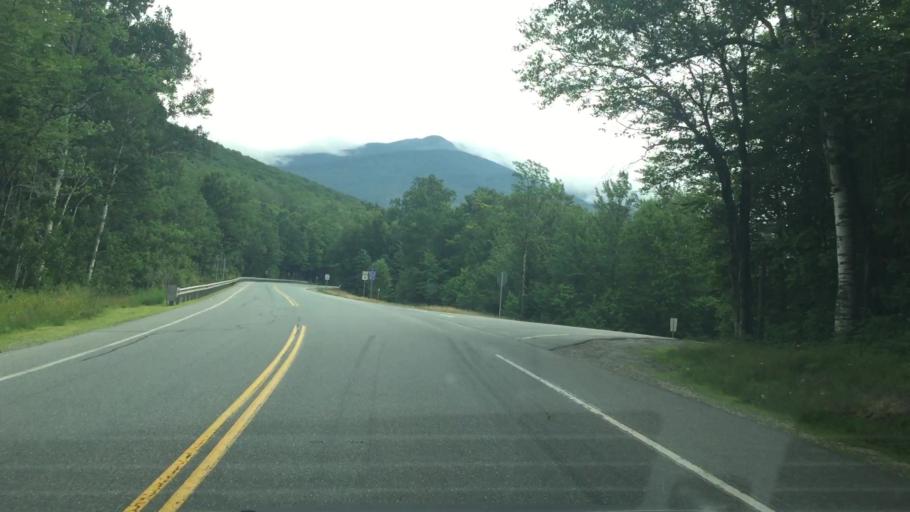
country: US
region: New Hampshire
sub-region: Grafton County
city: Deerfield
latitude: 44.2072
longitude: -71.6841
